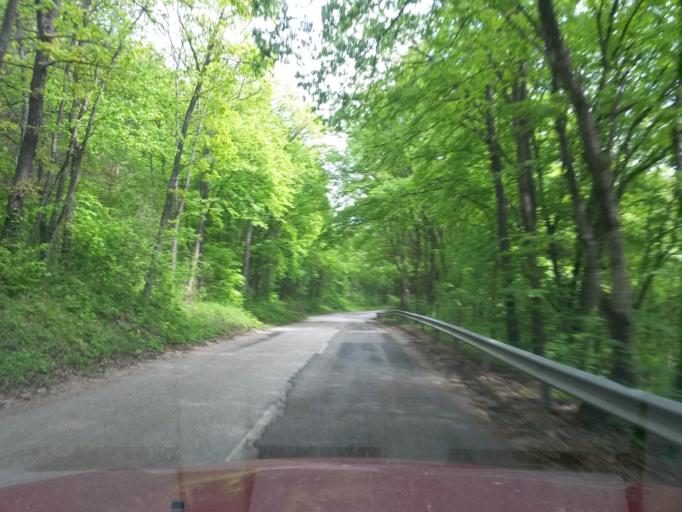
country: SK
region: Kosicky
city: Roznava
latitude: 48.5602
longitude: 20.4784
